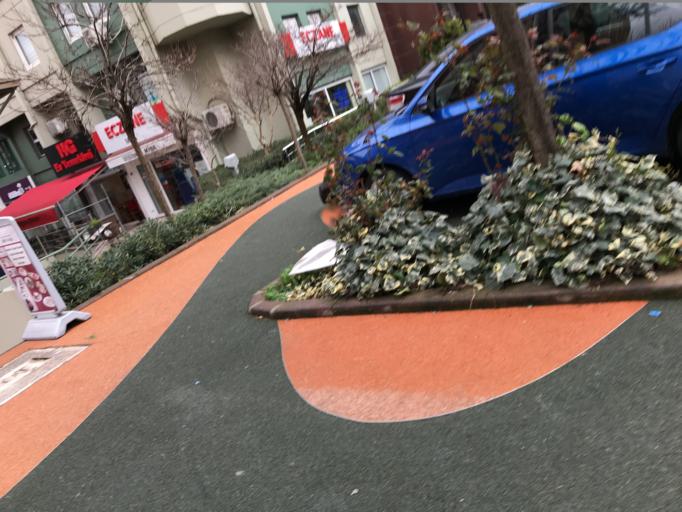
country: TR
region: Istanbul
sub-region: Atasehir
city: Atasehir
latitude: 40.9920
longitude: 29.1227
